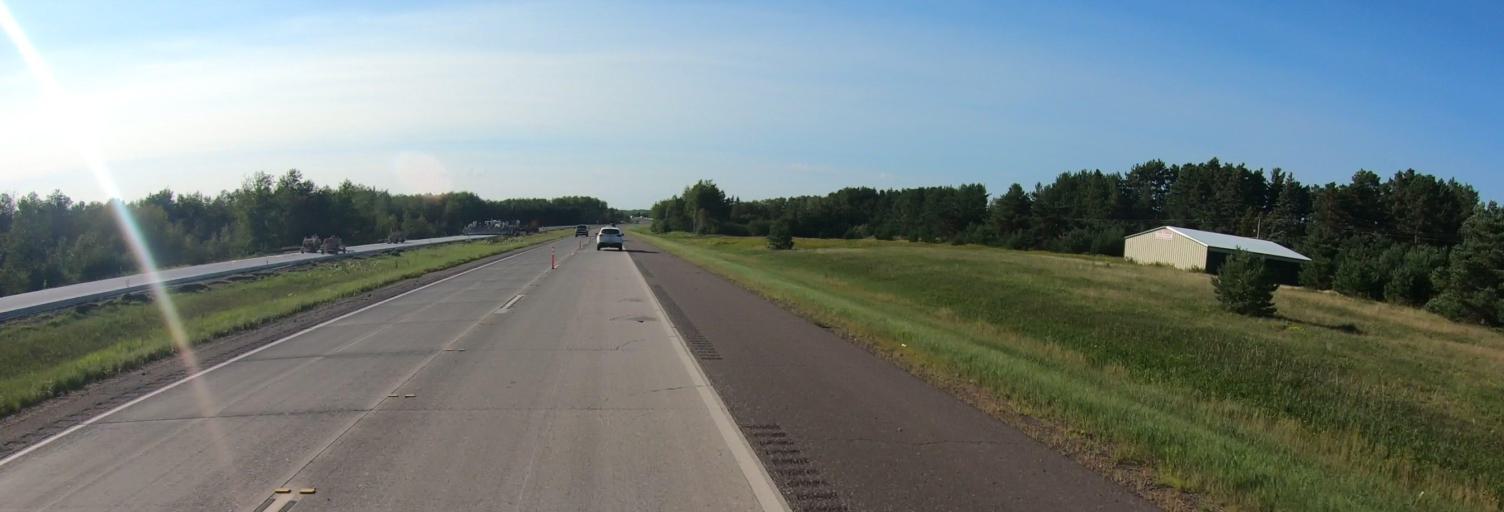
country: US
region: Minnesota
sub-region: Saint Louis County
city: Hermantown
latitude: 46.8703
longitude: -92.3354
